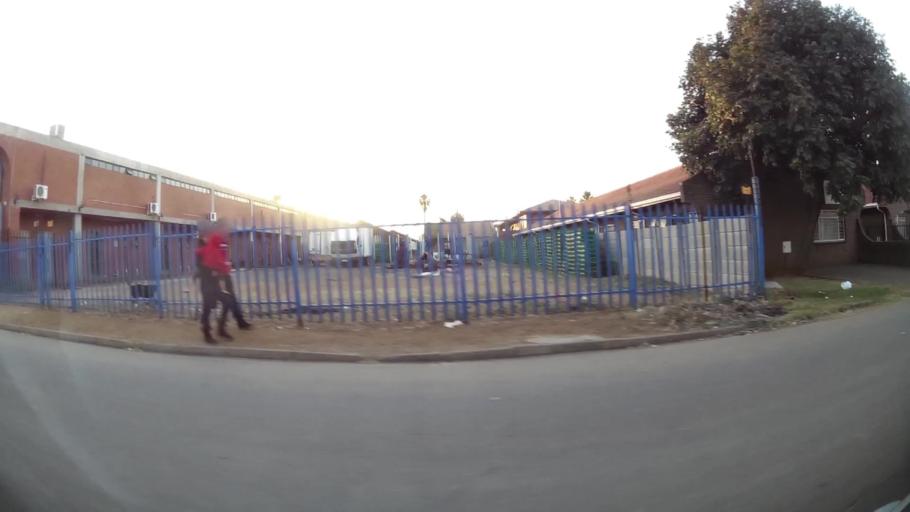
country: ZA
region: North-West
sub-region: Bojanala Platinum District Municipality
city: Rustenburg
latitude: -25.6668
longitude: 27.2443
